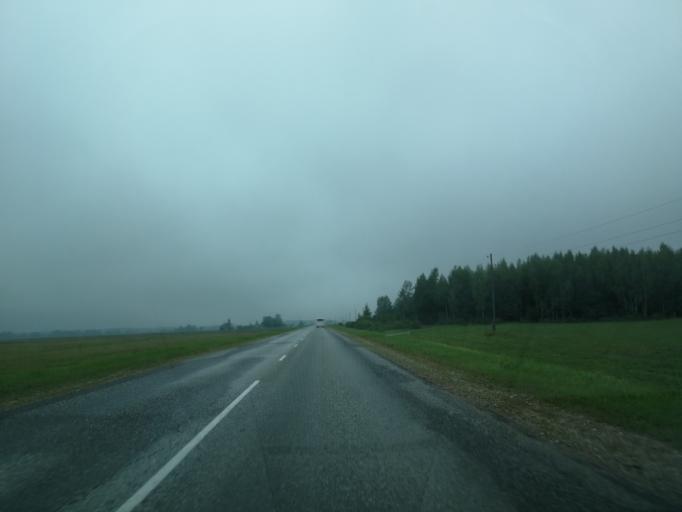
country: LV
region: Preilu Rajons
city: Preili
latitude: 56.3069
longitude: 26.5975
